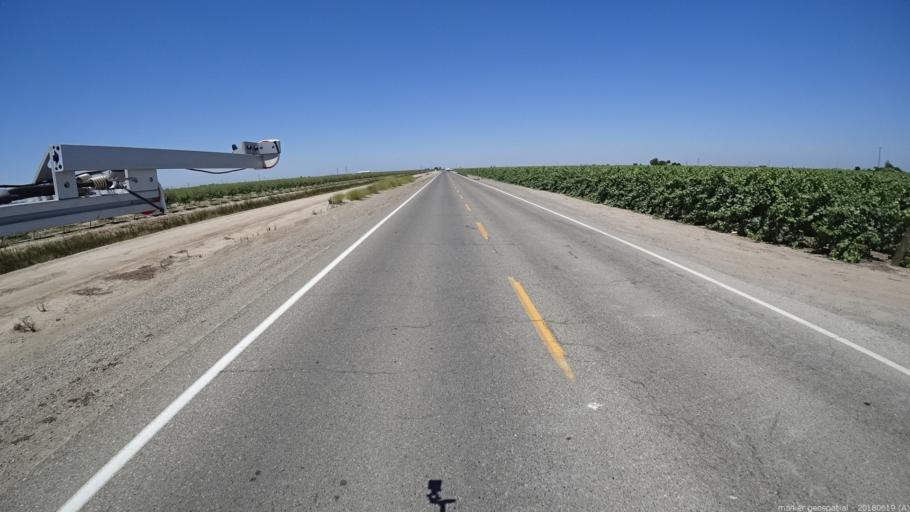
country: US
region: California
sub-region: Madera County
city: Parkwood
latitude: 36.8512
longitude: -120.1240
